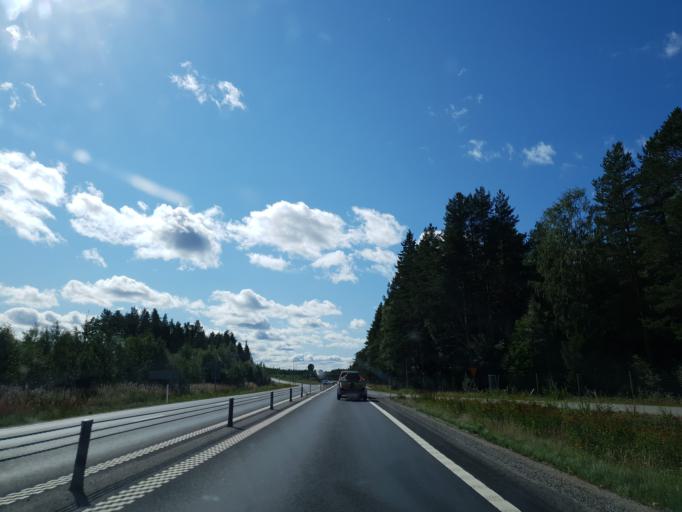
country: SE
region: Vaesterbotten
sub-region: Nordmalings Kommun
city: Nordmaling
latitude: 63.5526
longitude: 19.4182
